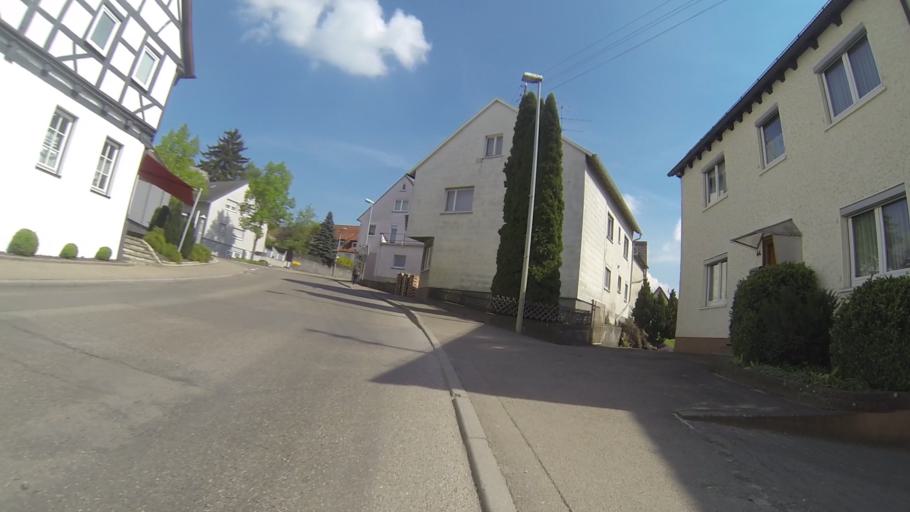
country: DE
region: Baden-Wuerttemberg
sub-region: Regierungsbezirk Stuttgart
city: Gerstetten
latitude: 48.6211
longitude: 10.0215
